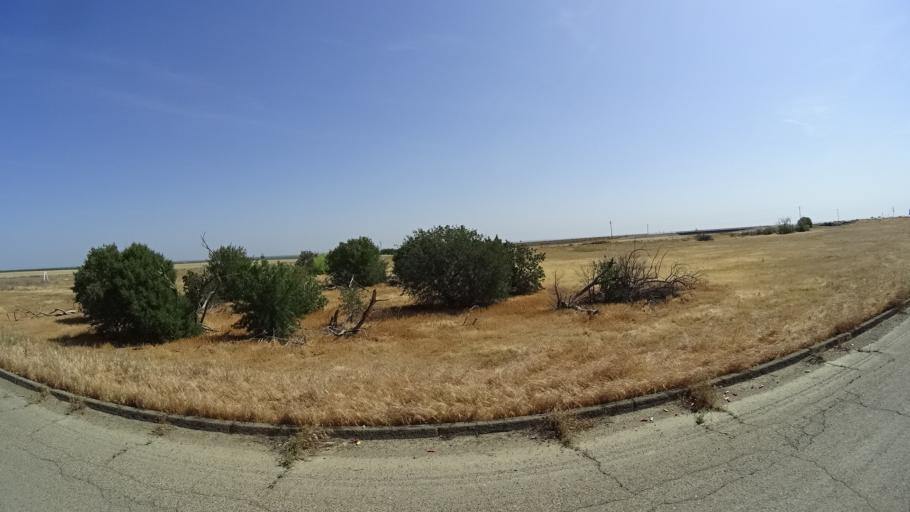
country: US
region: California
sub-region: Kings County
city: Kettleman City
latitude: 36.0477
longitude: -120.0070
